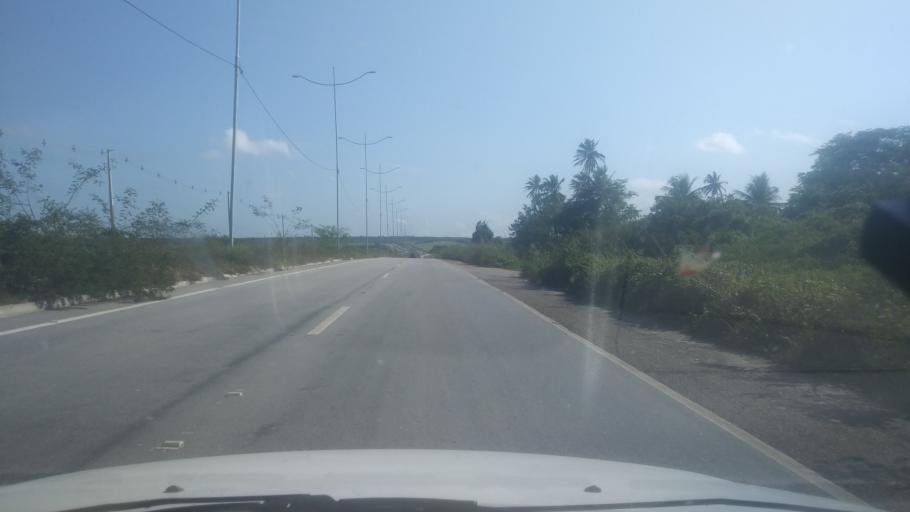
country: BR
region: Rio Grande do Norte
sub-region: Sao Goncalo Do Amarante
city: Sao Goncalo do Amarante
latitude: -5.8072
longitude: -35.3606
